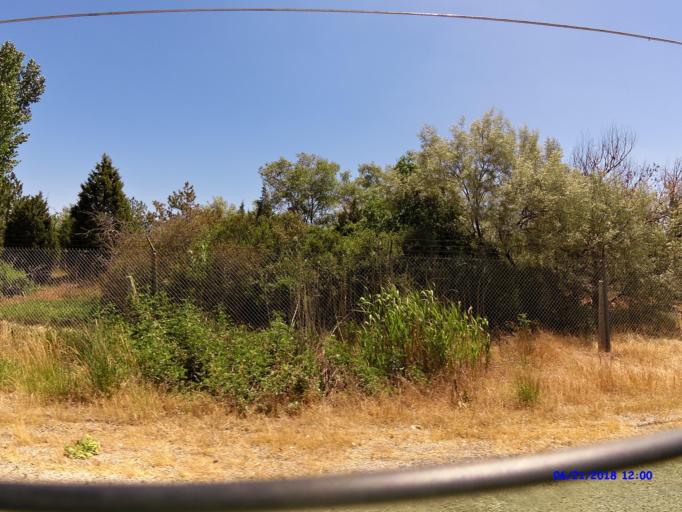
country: US
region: Utah
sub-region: Weber County
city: Marriott-Slaterville
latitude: 41.2519
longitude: -112.0096
